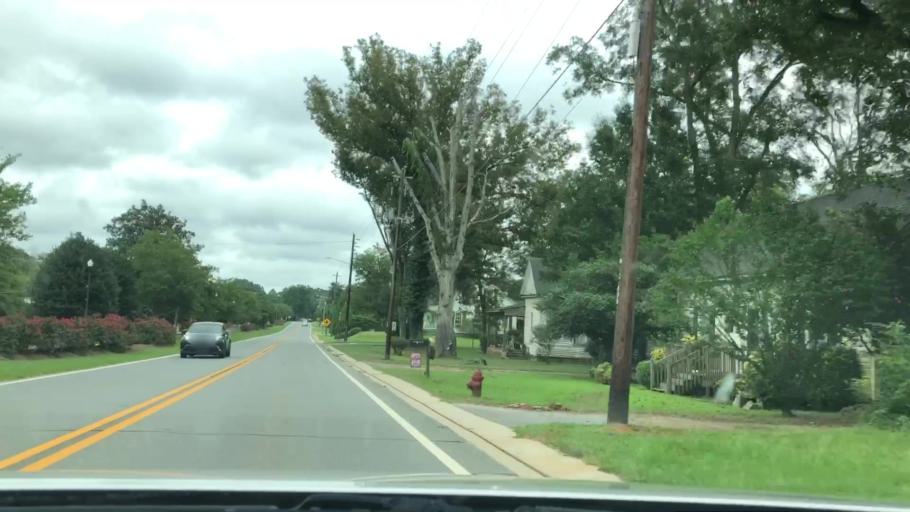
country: US
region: Georgia
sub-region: Pike County
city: Zebulon
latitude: 33.0897
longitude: -84.4428
